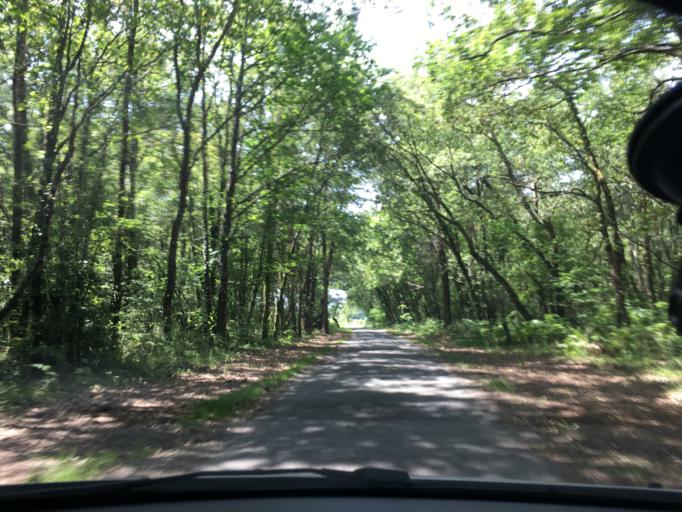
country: FR
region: Aquitaine
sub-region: Departement de la Gironde
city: Lesparre-Medoc
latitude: 45.2792
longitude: -0.9106
